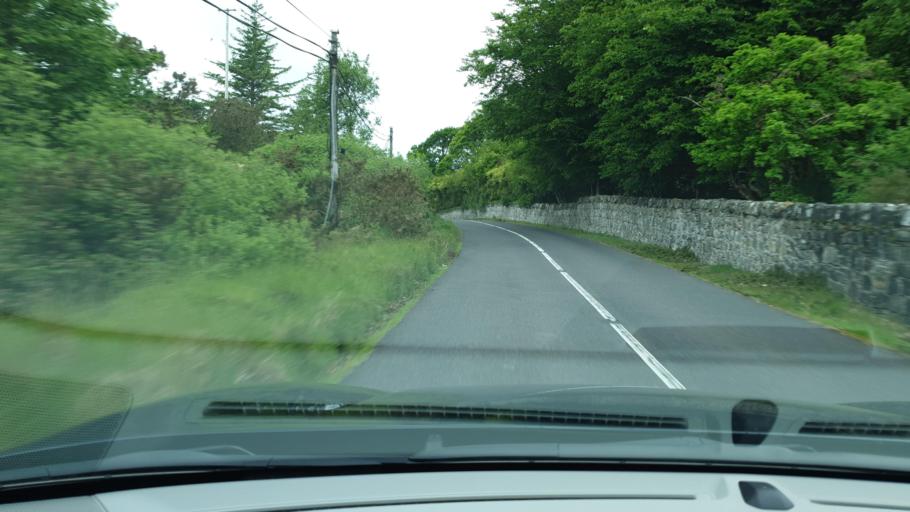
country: IE
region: Connaught
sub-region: County Galway
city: Clifden
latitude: 53.4587
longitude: -9.8118
